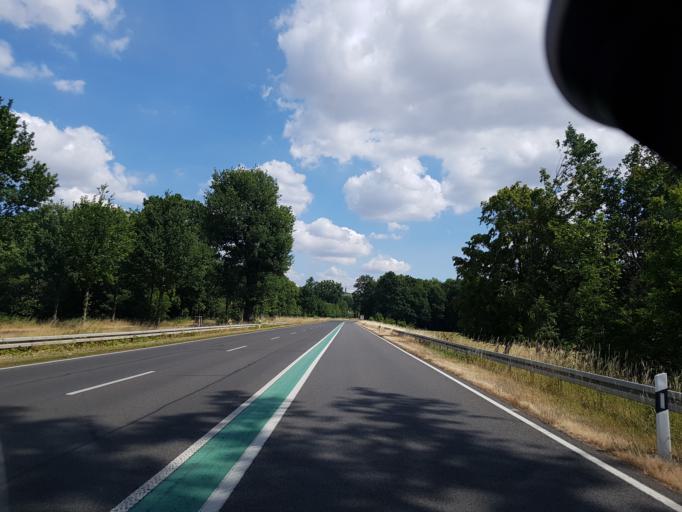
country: DE
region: Brandenburg
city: Drebkau
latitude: 51.6880
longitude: 14.2634
